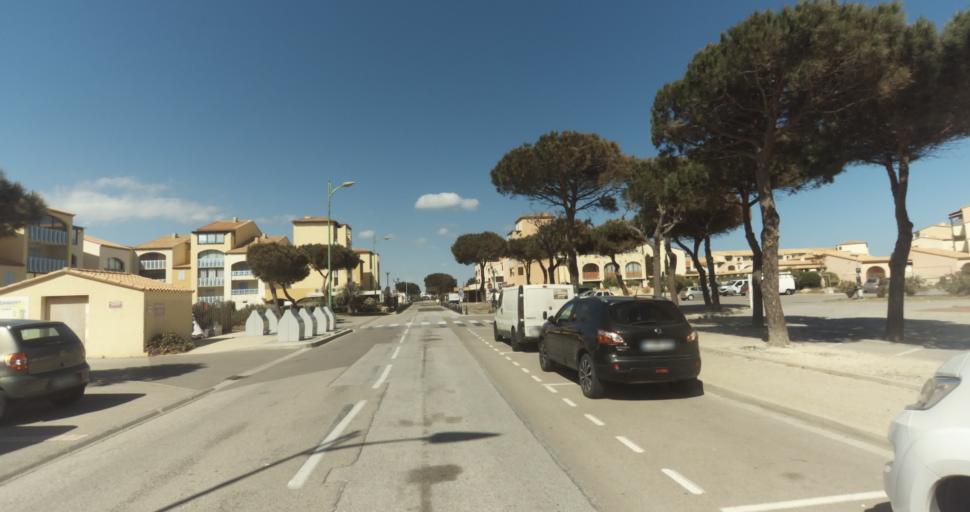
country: FR
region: Languedoc-Roussillon
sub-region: Departement des Pyrenees-Orientales
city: Le Barcares
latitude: 42.8329
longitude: 3.0397
